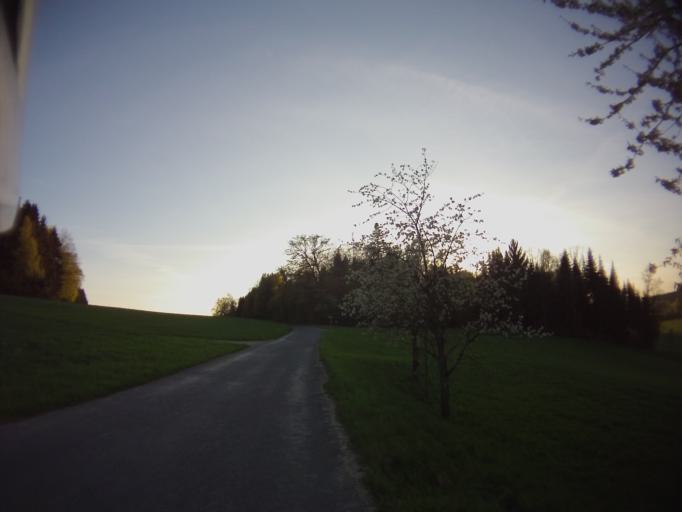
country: CH
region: Zurich
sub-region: Bezirk Affoltern
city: Knonau
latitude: 47.2195
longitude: 8.4569
